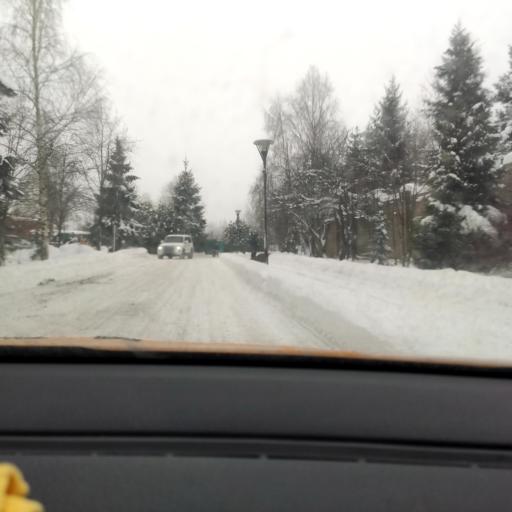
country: RU
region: Moskovskaya
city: Zarech'ye
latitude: 55.6776
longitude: 37.3938
